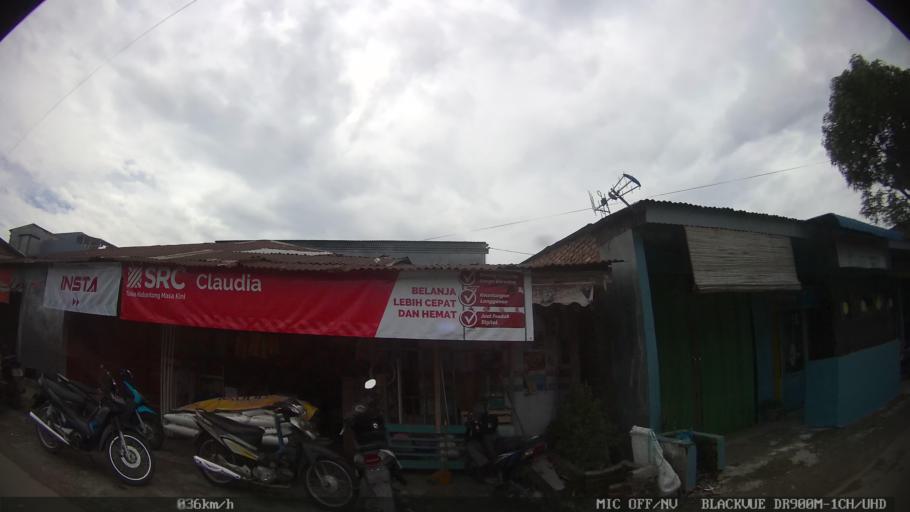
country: ID
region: North Sumatra
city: Sunggal
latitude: 3.5983
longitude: 98.5662
